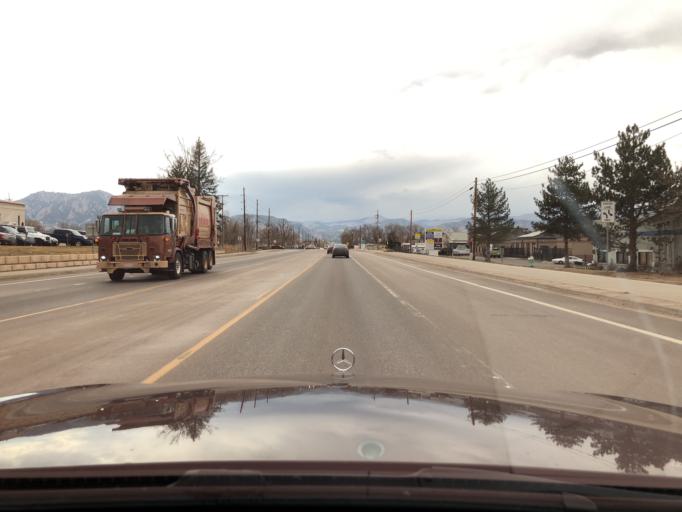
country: US
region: Colorado
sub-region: Boulder County
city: Gunbarrel
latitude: 40.0147
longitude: -105.2012
